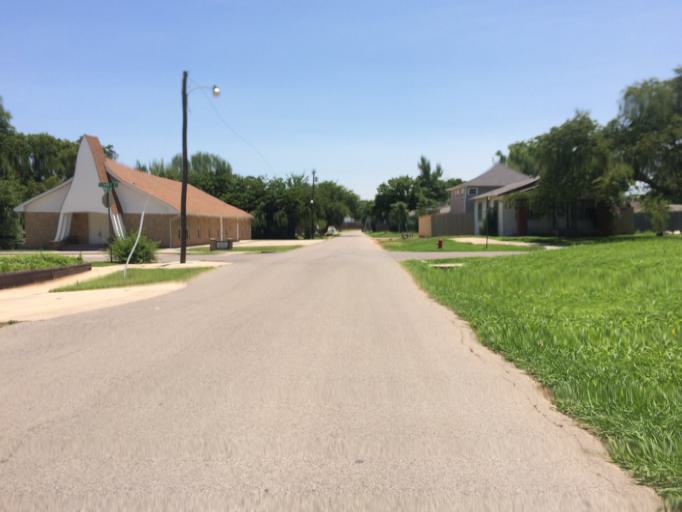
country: US
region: Oklahoma
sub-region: Cleveland County
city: Norman
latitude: 35.2207
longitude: -97.4362
